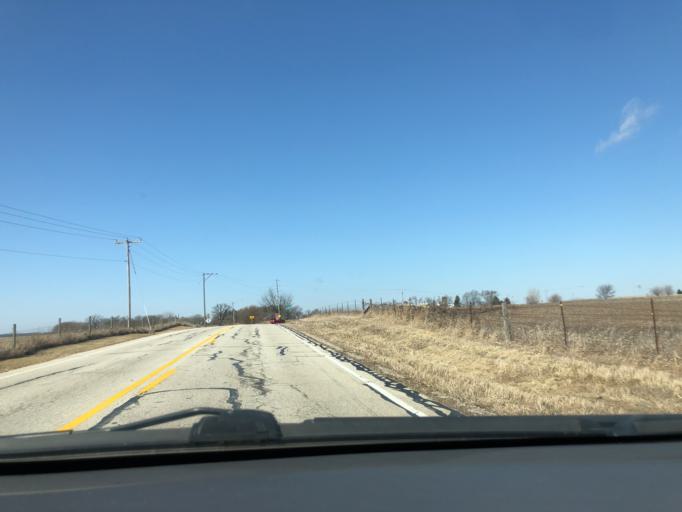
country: US
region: Illinois
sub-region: Kane County
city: Hampshire
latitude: 42.1347
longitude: -88.5330
